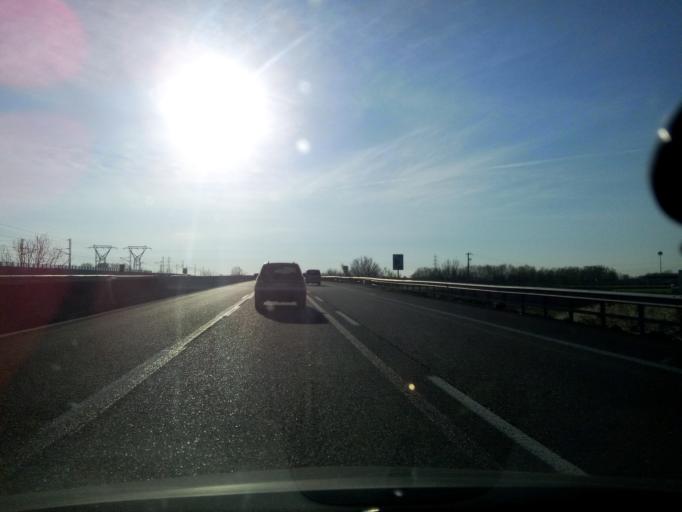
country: IT
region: Emilia-Romagna
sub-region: Provincia di Parma
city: Baganzola
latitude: 44.8482
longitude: 10.3041
